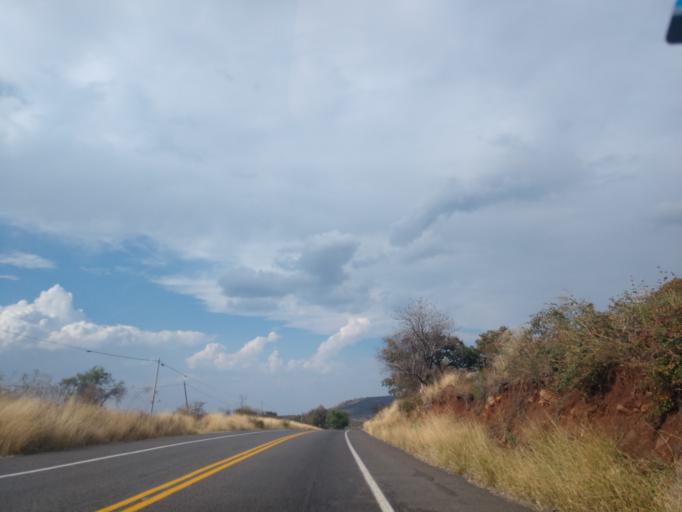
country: MX
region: Jalisco
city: La Manzanilla de la Paz
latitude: 20.0730
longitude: -103.1709
